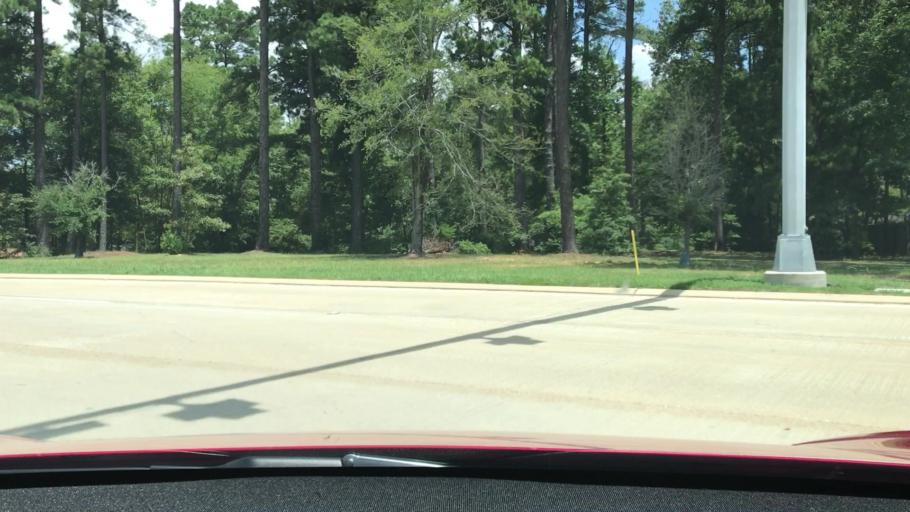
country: US
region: Louisiana
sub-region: Bossier Parish
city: Bossier City
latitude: 32.3967
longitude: -93.7288
